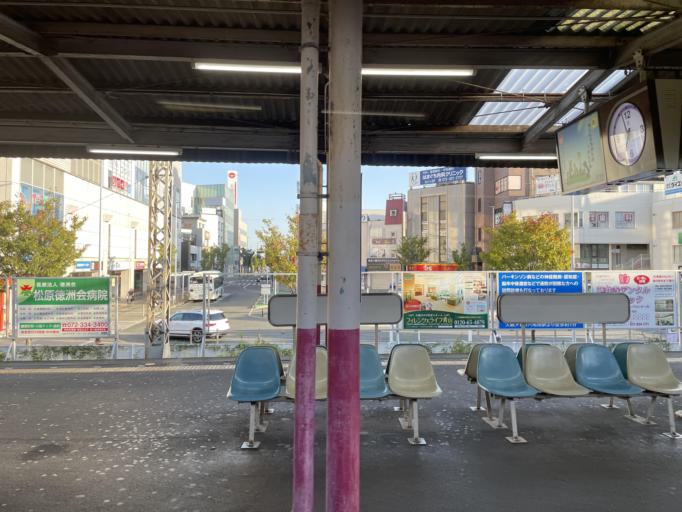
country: JP
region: Osaka
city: Kashihara
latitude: 34.5717
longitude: 135.5939
